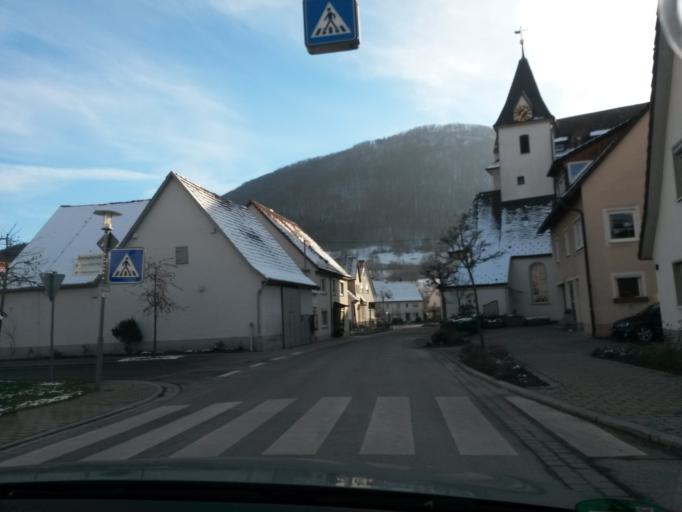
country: DE
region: Baden-Wuerttemberg
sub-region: Regierungsbezirk Stuttgart
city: Bad Uberkingen
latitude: 48.6070
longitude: 9.7633
